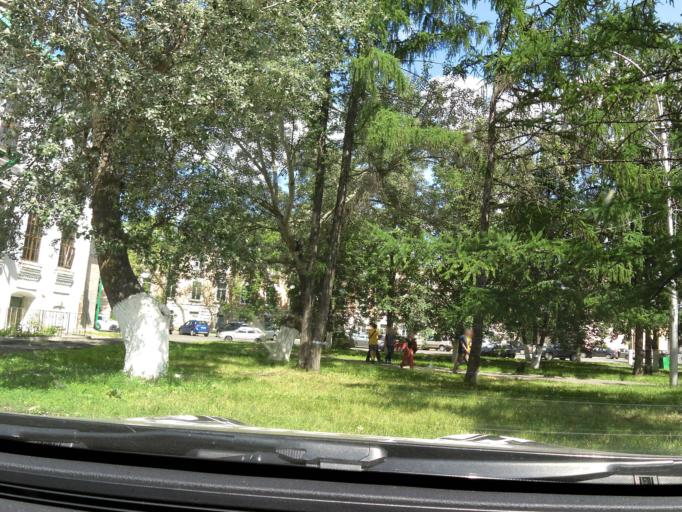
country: RU
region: Vologda
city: Vologda
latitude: 59.2233
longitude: 39.8869
